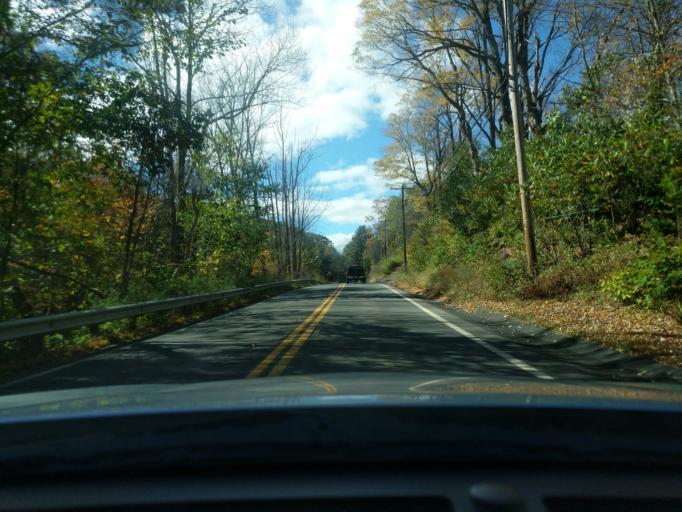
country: US
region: Massachusetts
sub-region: Hampden County
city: Granville
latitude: 42.1700
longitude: -72.8925
